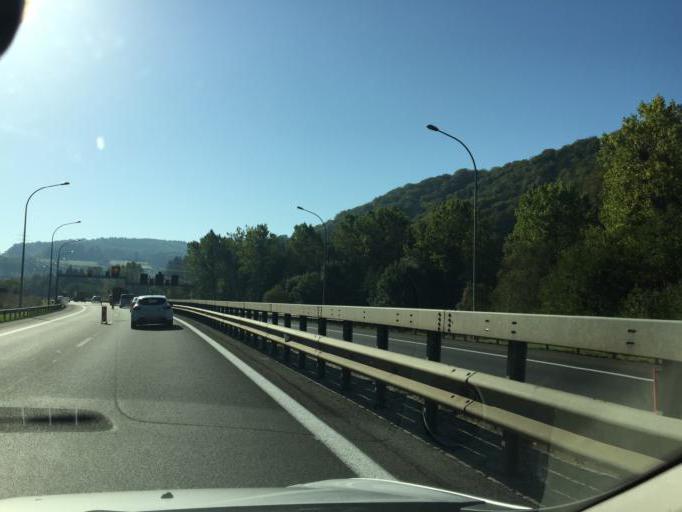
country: LU
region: Luxembourg
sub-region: Canton de Mersch
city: Mersch
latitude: 49.7361
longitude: 6.0982
